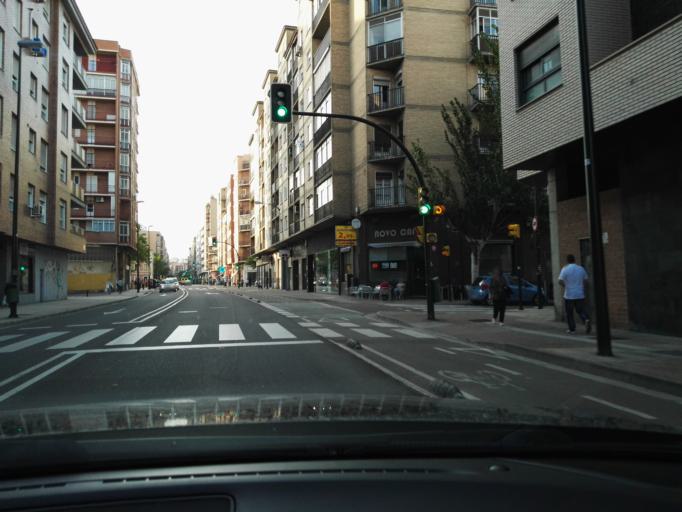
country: ES
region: Aragon
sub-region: Provincia de Zaragoza
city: Zaragoza
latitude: 41.6397
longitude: -0.8661
